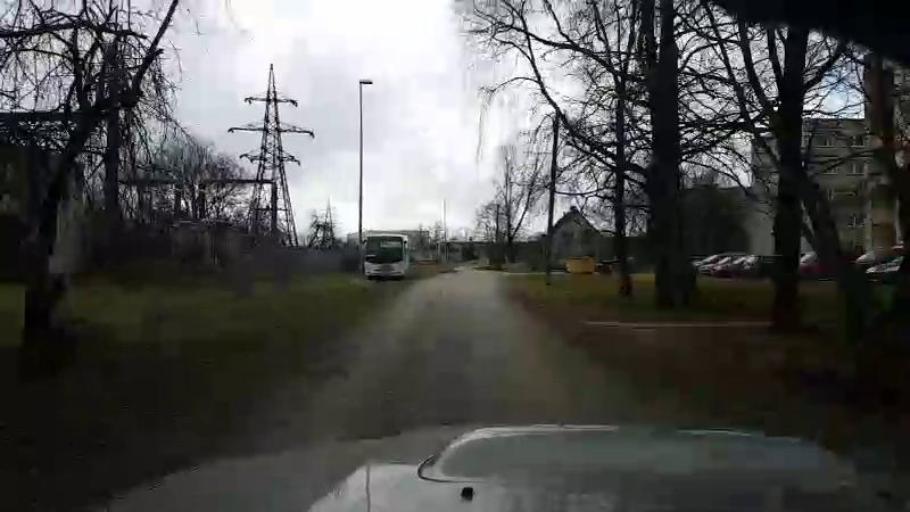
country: EE
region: Jaervamaa
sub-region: Paide linn
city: Paide
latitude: 58.8844
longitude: 25.5627
